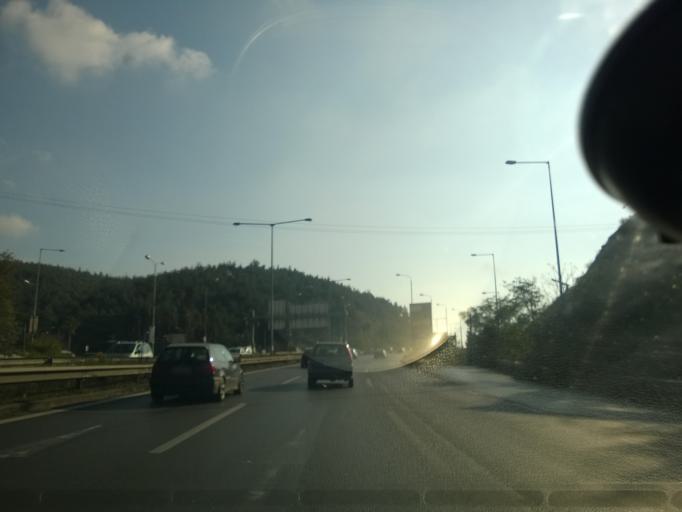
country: GR
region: Central Macedonia
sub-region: Nomos Thessalonikis
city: Polichni
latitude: 40.6607
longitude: 22.9682
